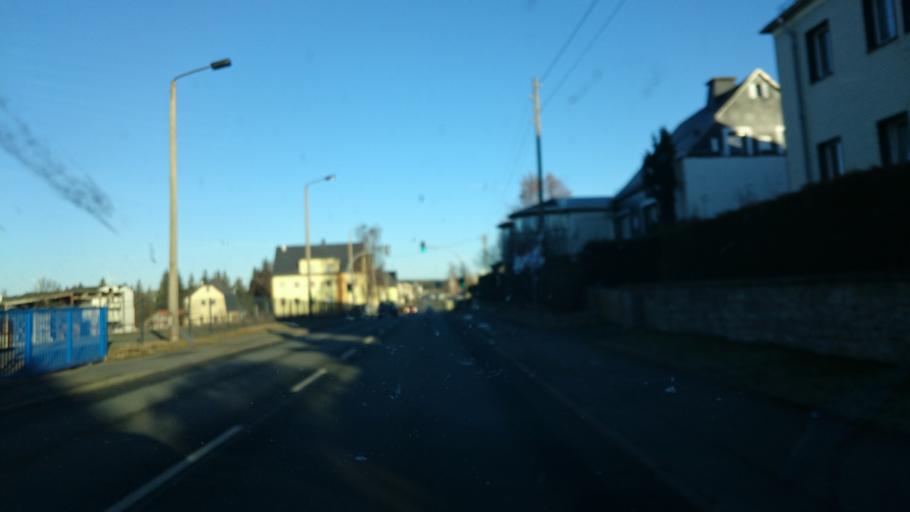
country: DE
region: Thuringia
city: Schleiz
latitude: 50.5781
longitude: 11.8179
